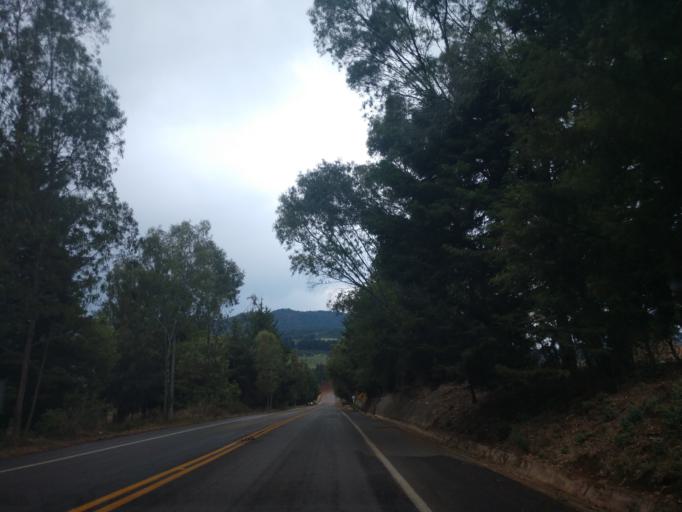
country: MX
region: Jalisco
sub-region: Mazamitla
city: Mazamitla
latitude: 19.9357
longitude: -103.0518
